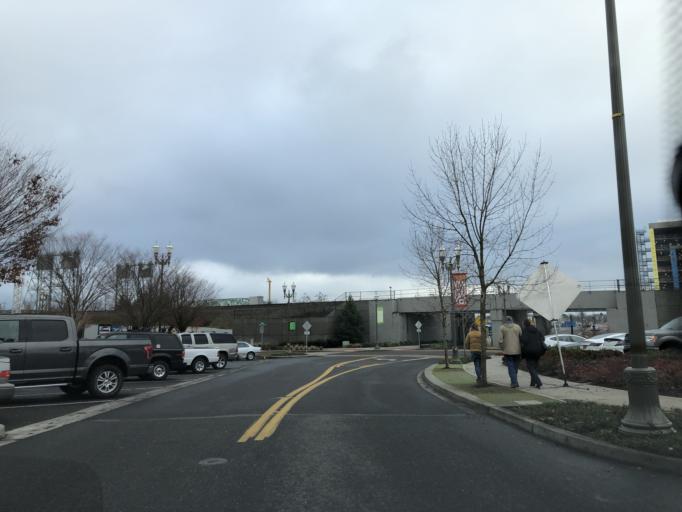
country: US
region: Washington
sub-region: Clark County
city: Vancouver
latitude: 45.6249
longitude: -122.6761
